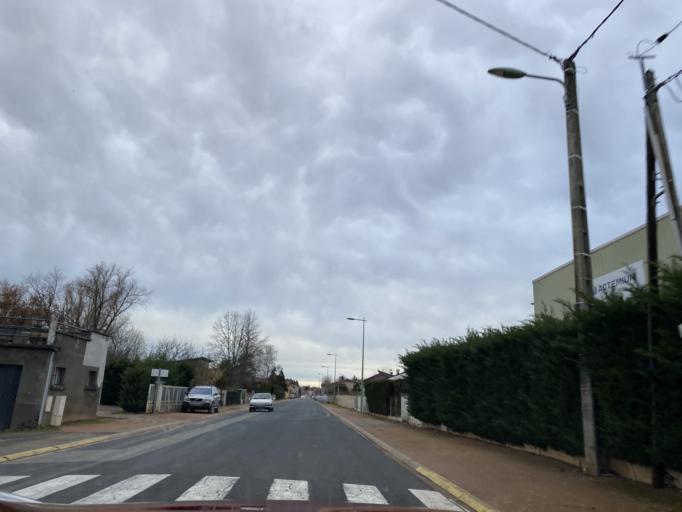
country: FR
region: Auvergne
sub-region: Departement du Puy-de-Dome
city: Peschadoires
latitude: 45.8318
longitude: 3.5006
